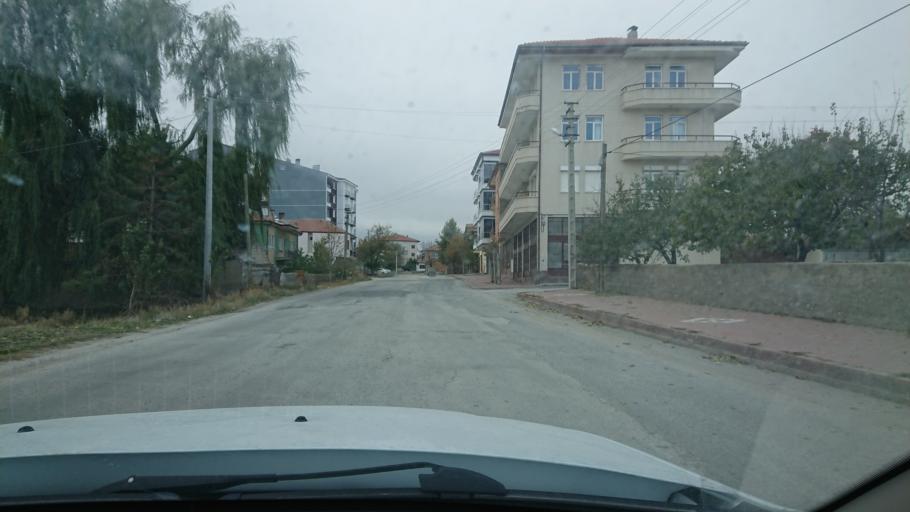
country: TR
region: Aksaray
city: Ortakoy
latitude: 38.7440
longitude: 34.0476
